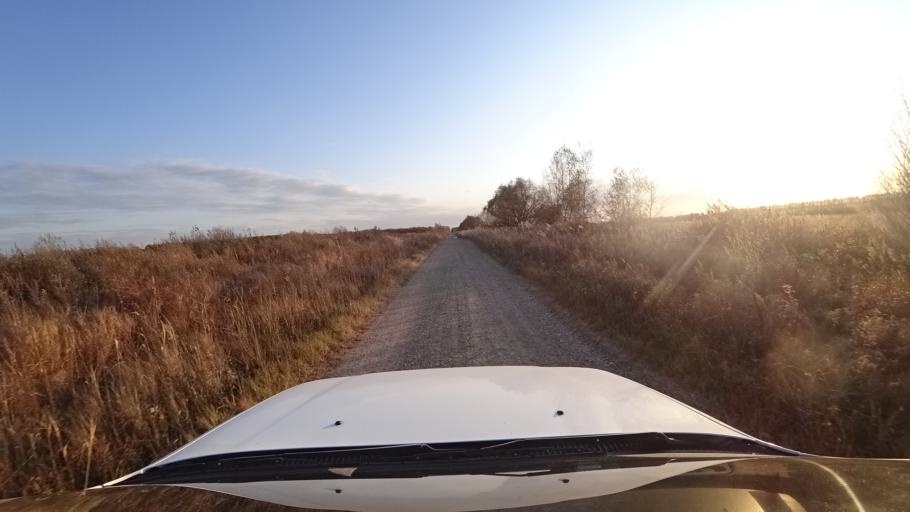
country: RU
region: Primorskiy
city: Lazo
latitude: 45.8120
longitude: 133.6088
